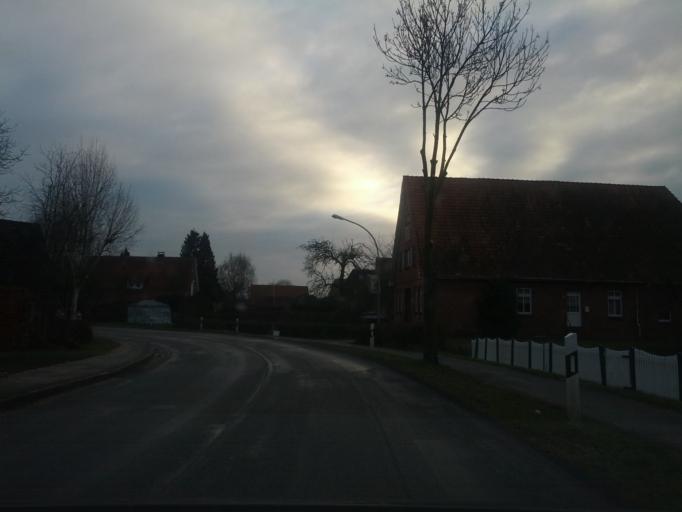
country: DE
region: Lower Saxony
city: Grunendeich
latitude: 53.5768
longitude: 9.6034
